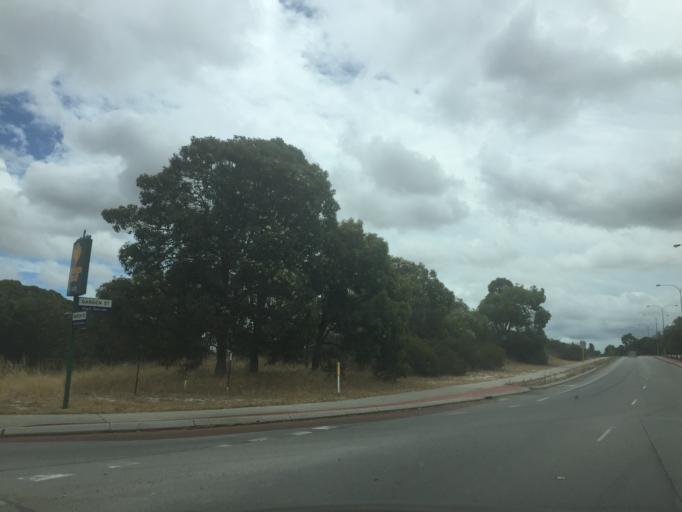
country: AU
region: Western Australia
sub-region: Gosnells
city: Thornlie
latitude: -32.0827
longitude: 115.9515
